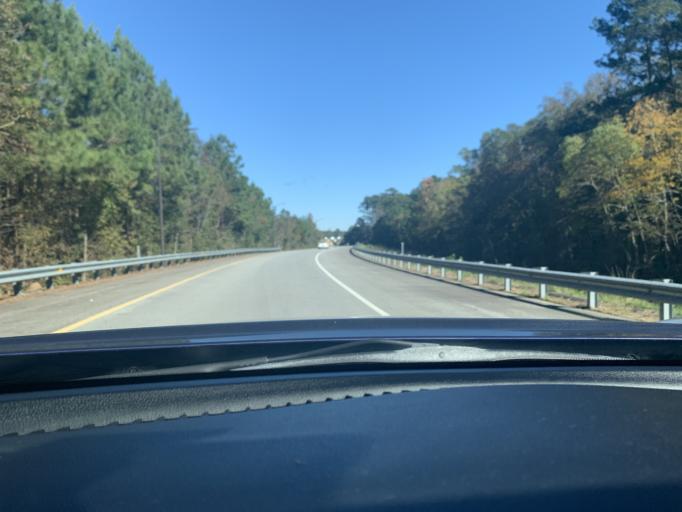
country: US
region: Georgia
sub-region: Chatham County
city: Pooler
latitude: 32.1168
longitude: -81.2679
